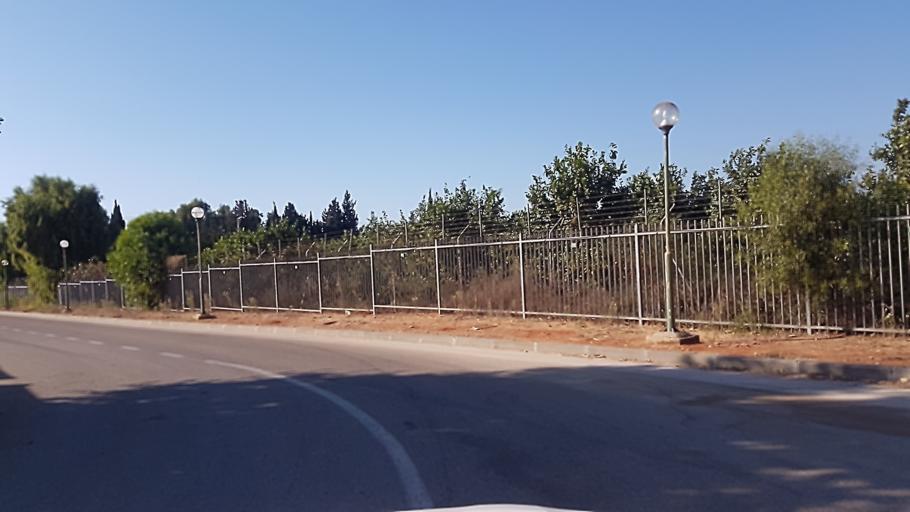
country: IL
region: Central District
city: Kfar Saba
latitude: 32.2012
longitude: 34.9194
